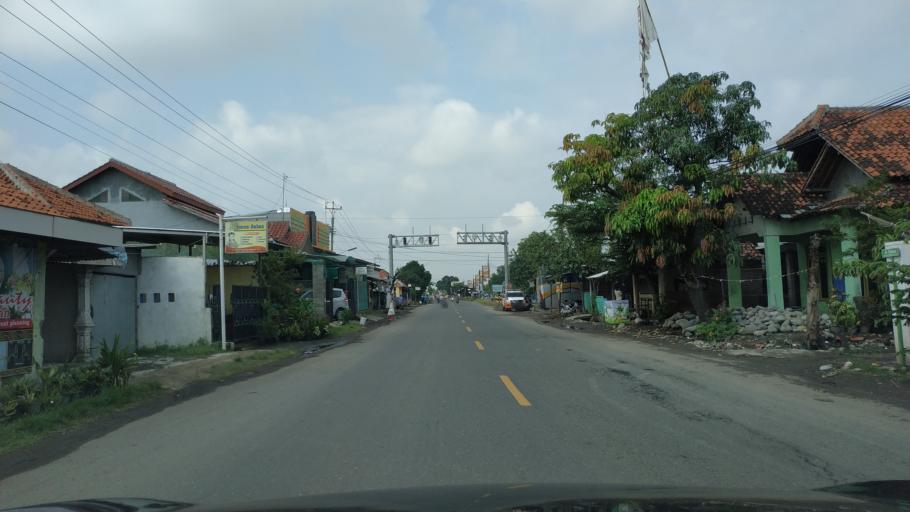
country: ID
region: Central Java
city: Ketanggungan
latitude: -6.8771
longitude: 108.8856
